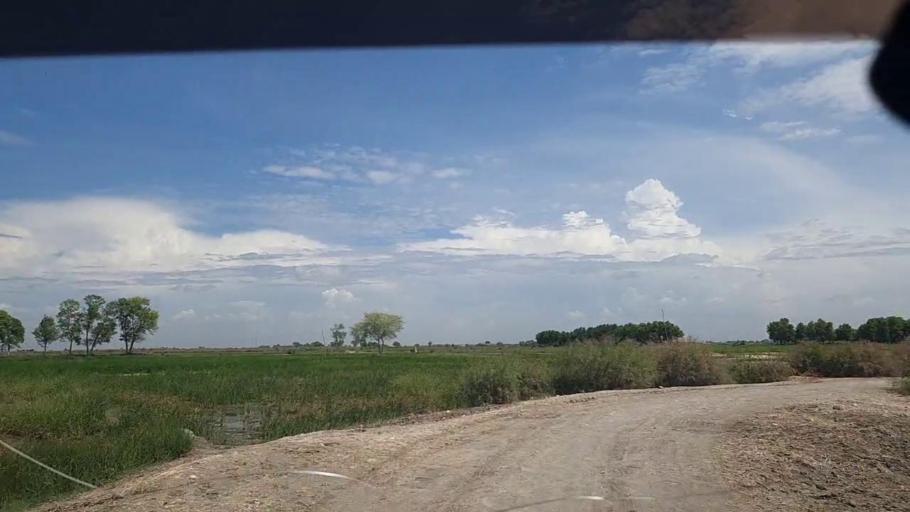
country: PK
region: Sindh
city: Ghauspur
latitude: 28.1494
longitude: 68.9667
